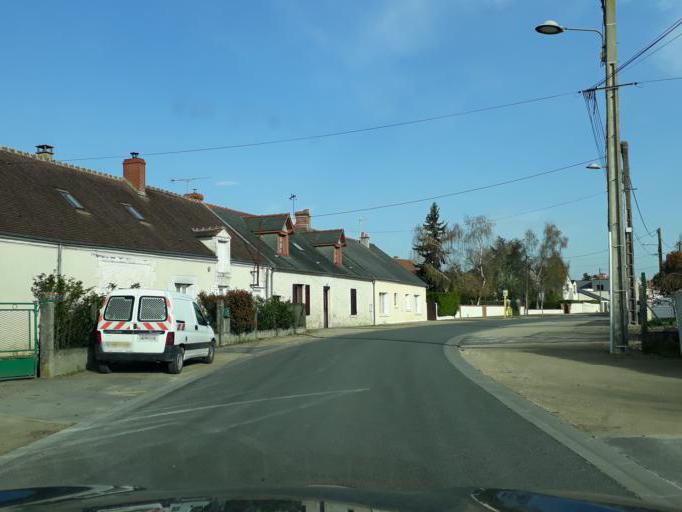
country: FR
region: Centre
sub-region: Departement du Loiret
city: Ingre
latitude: 47.9155
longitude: 1.8091
